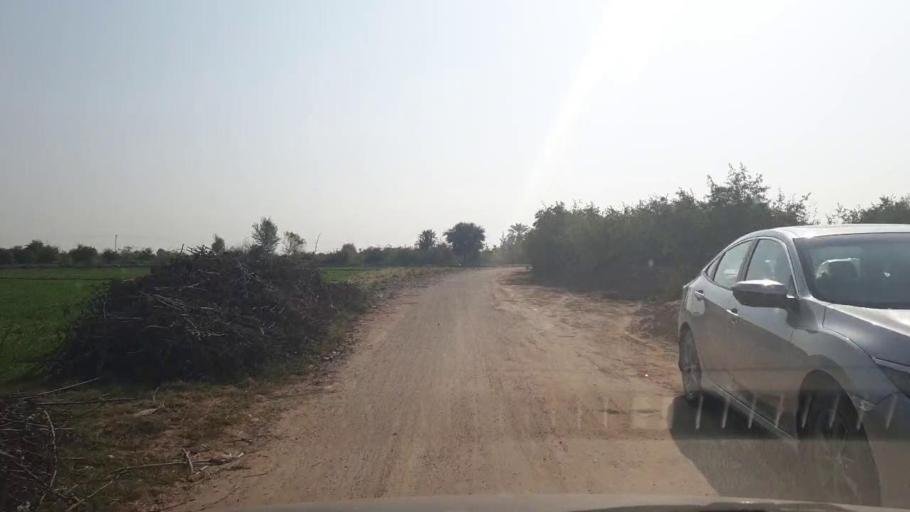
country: PK
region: Sindh
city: Bhit Shah
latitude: 25.8139
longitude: 68.5742
